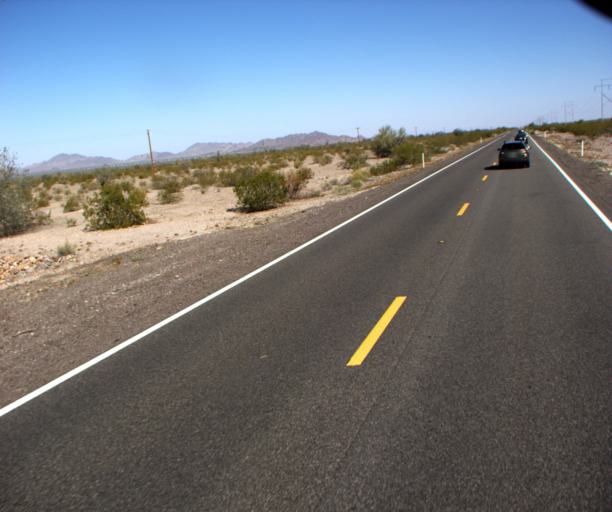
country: US
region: Arizona
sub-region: La Paz County
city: Quartzsite
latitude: 33.5622
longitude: -114.2170
